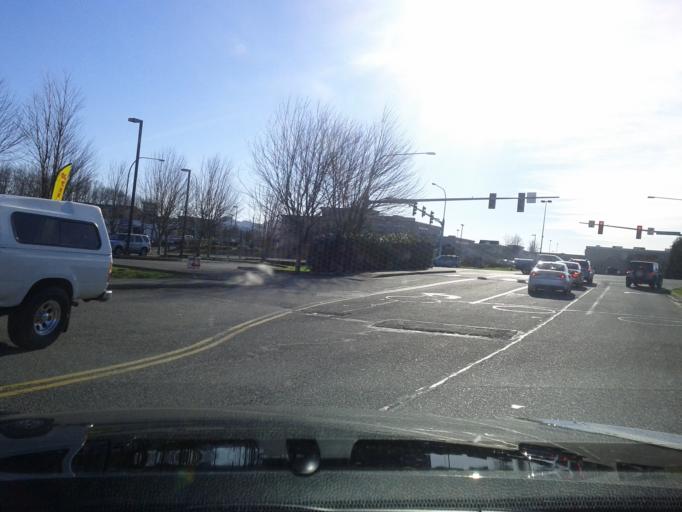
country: US
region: Washington
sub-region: Skagit County
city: Burlington
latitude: 48.4527
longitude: -122.3375
